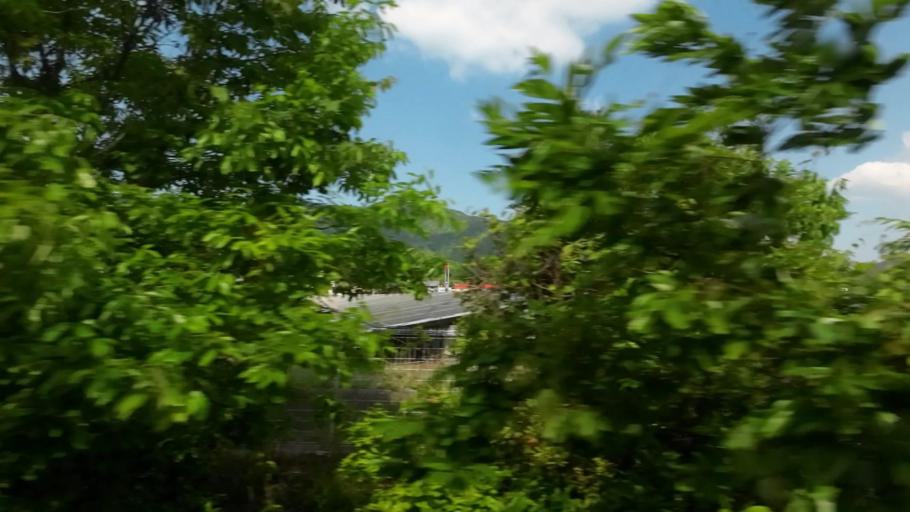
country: JP
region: Kagawa
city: Kan'onjicho
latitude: 34.1694
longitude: 133.6910
